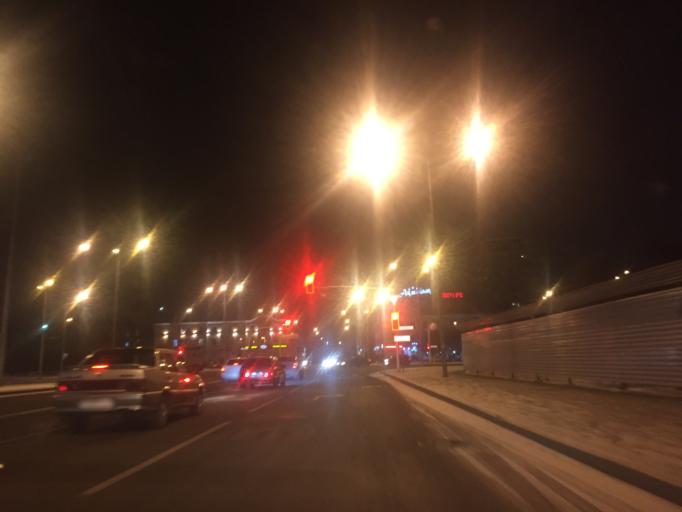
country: KZ
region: Astana Qalasy
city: Astana
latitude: 51.1912
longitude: 71.4077
